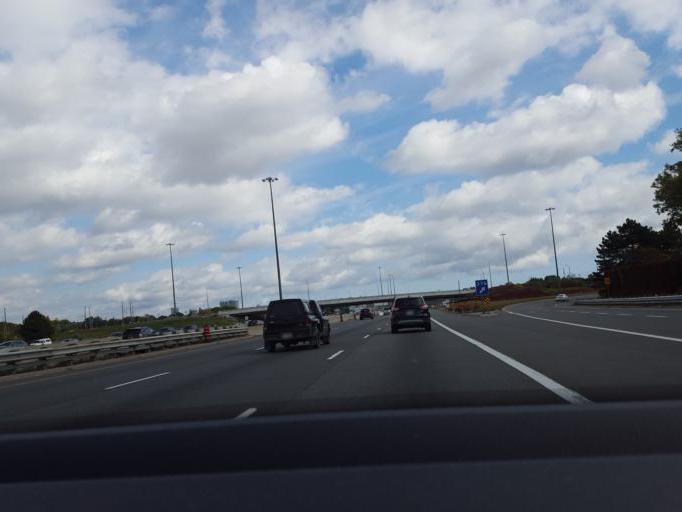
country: CA
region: Ontario
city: Scarborough
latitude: 43.7679
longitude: -79.3243
